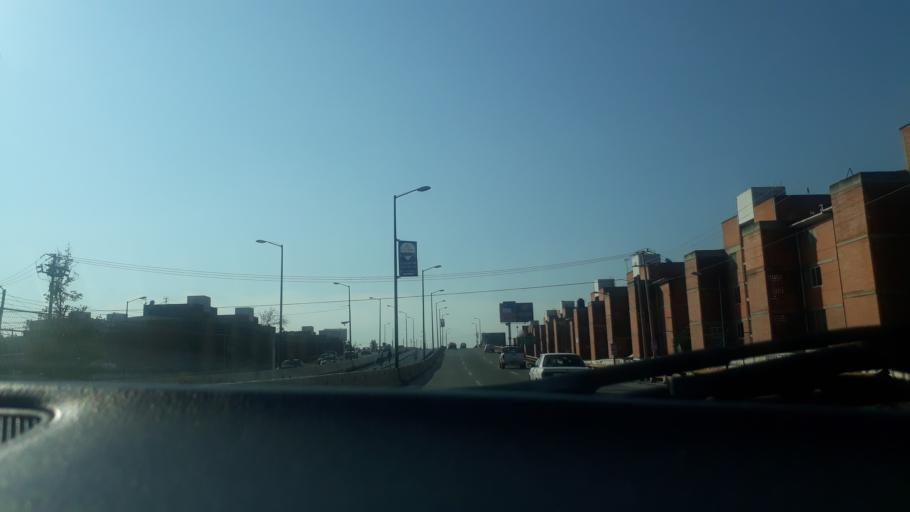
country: MX
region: Puebla
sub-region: Puebla
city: El Capulo (La Quebradora)
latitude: 18.9909
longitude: -98.2428
